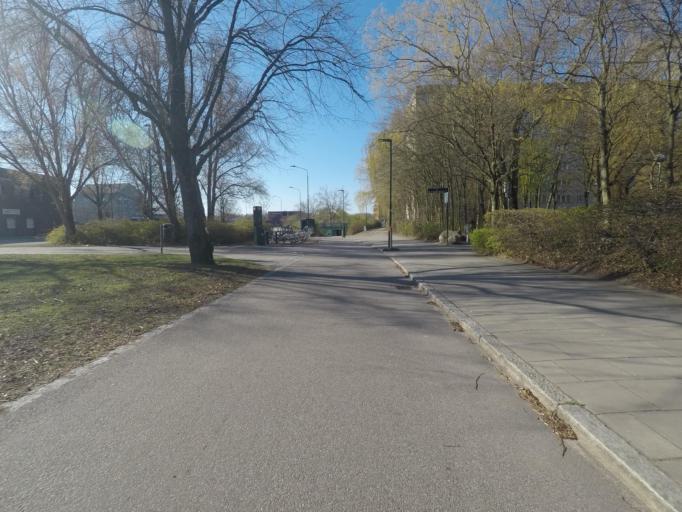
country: SE
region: Skane
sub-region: Malmo
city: Tygelsjo
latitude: 55.5598
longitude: 13.0130
